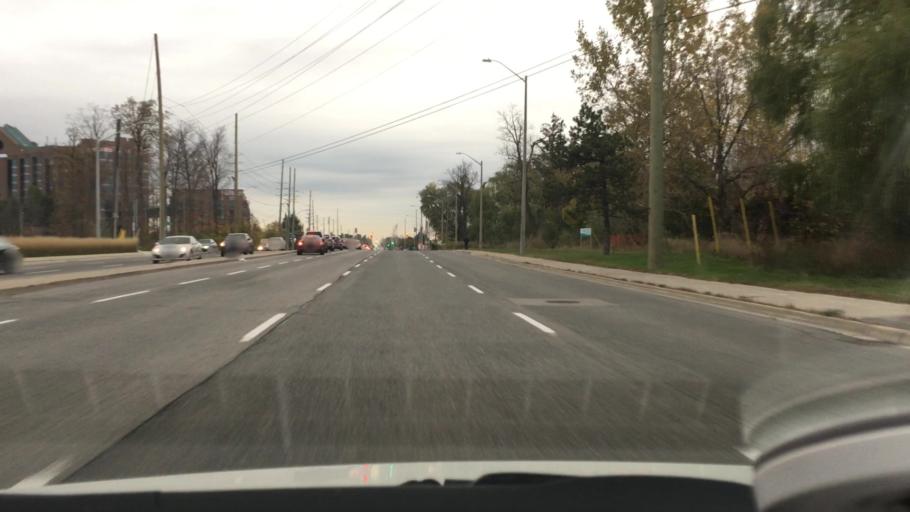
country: CA
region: Ontario
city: Markham
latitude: 43.8514
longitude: -79.3328
